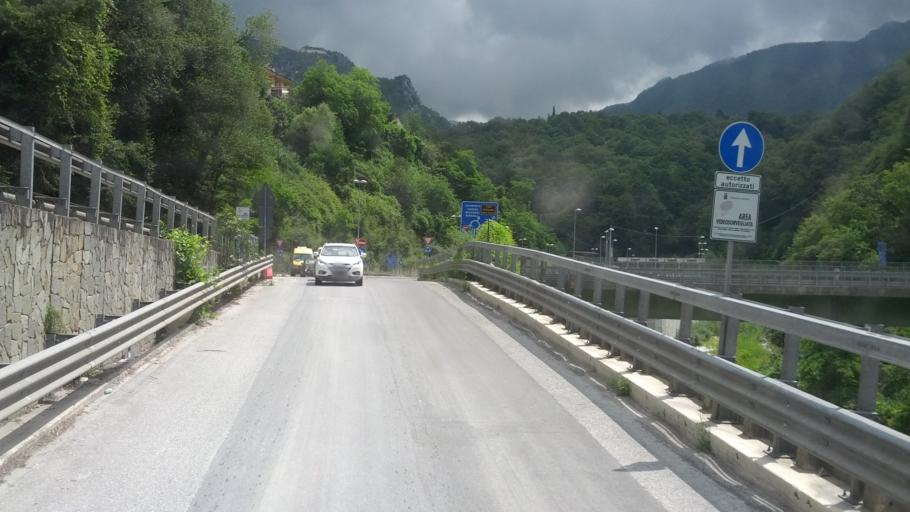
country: IT
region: Tuscany
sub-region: Provincia di Massa-Carrara
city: Carrara
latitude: 44.0820
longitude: 10.1134
